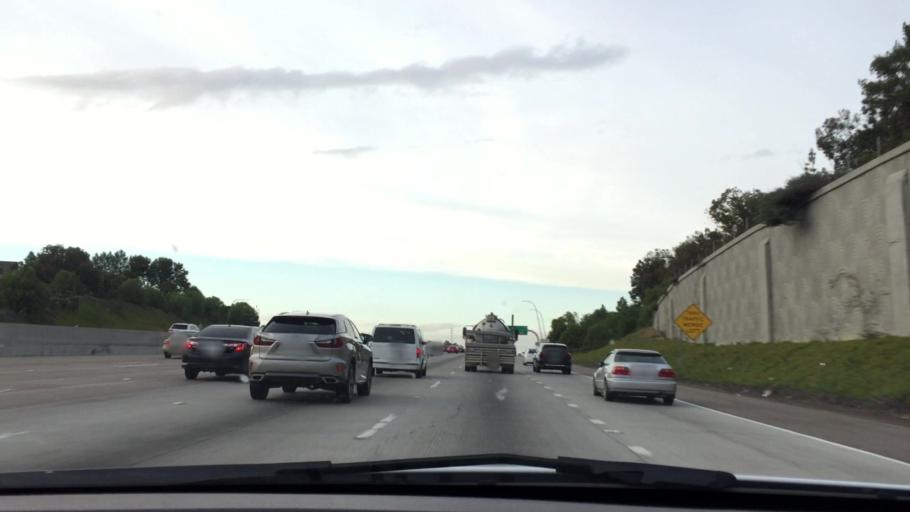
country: US
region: California
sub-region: San Diego County
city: Poway
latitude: 32.9905
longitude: -117.0829
